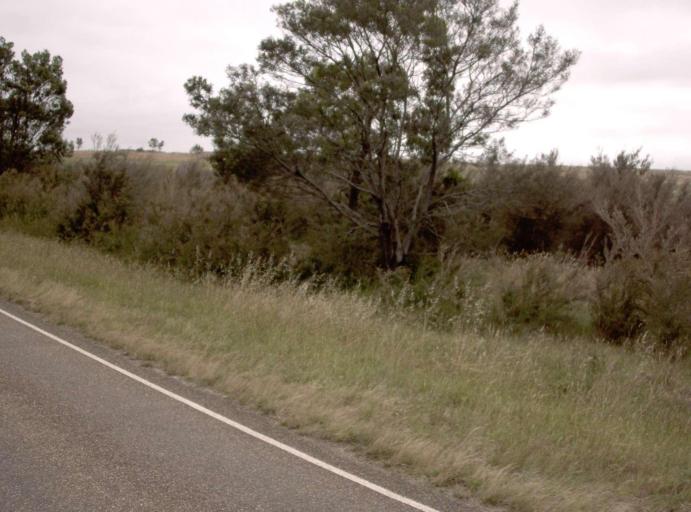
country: AU
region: Victoria
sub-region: Wellington
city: Heyfield
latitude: -38.1307
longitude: 146.7877
